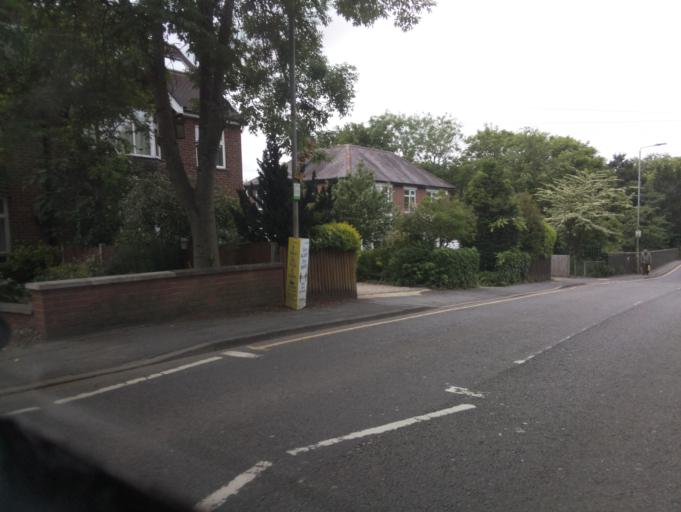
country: GB
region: England
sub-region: Leicestershire
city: Melton Mowbray
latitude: 52.7605
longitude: -0.8898
